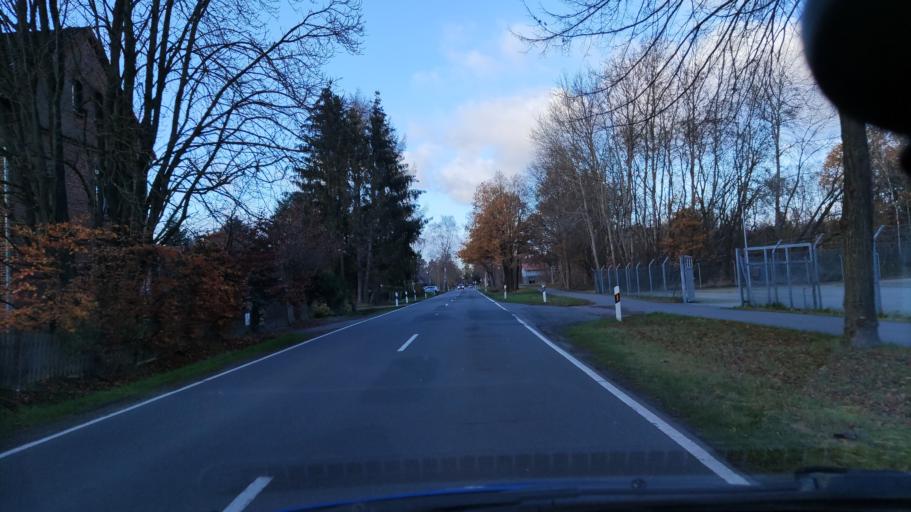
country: DE
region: Lower Saxony
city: Schneverdingen
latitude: 53.0763
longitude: 9.8125
